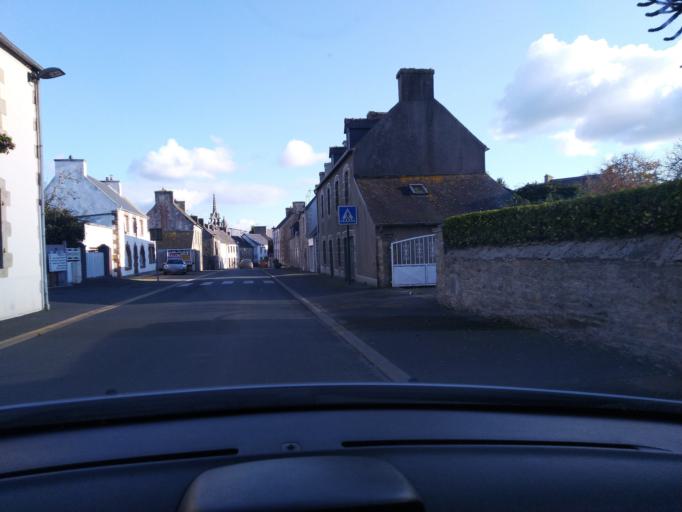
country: FR
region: Brittany
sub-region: Departement des Cotes-d'Armor
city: Plestin-les-Greves
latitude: 48.6043
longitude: -3.6124
